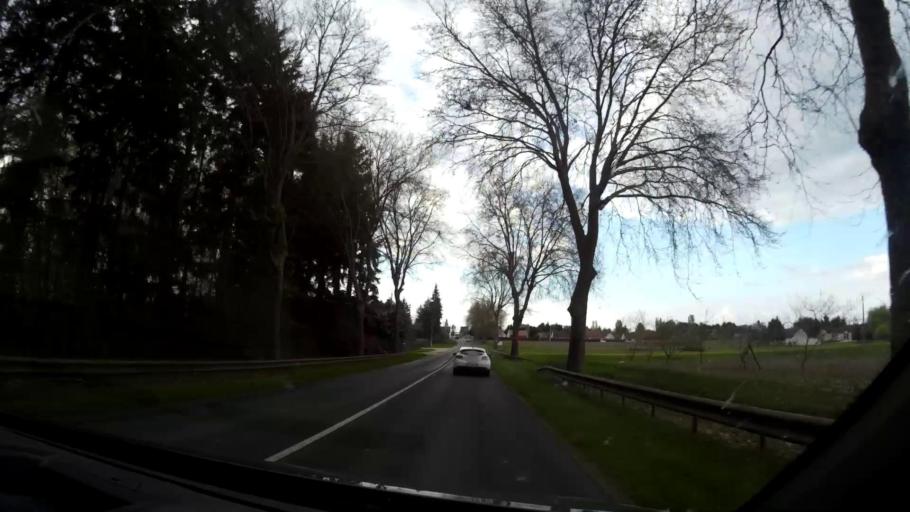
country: FR
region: Centre
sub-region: Departement du Loir-et-Cher
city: Cormeray
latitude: 47.4840
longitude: 1.4122
